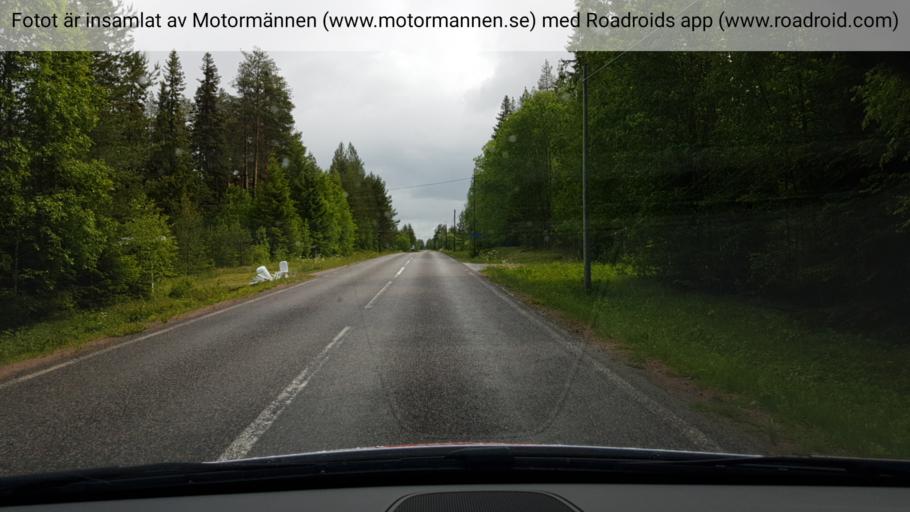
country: SE
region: Jaemtland
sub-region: Ragunda Kommun
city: Hammarstrand
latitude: 63.0248
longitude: 15.9599
